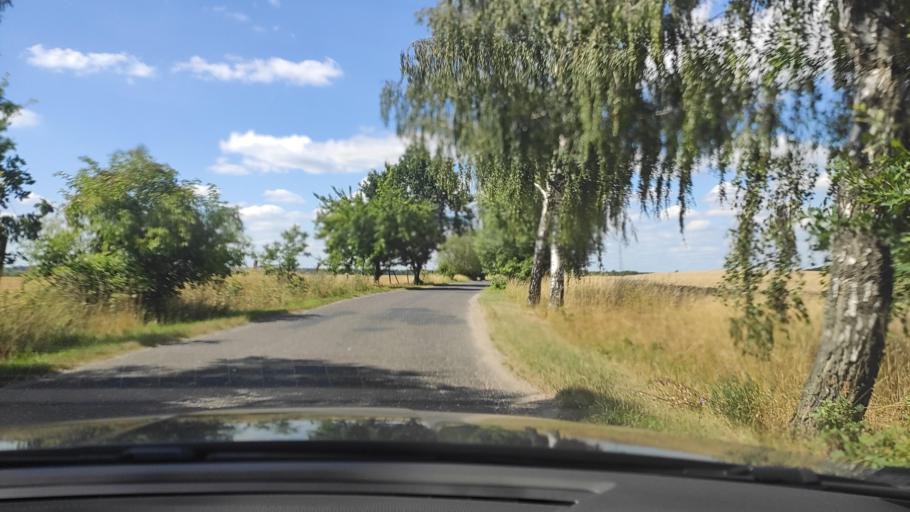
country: PL
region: Greater Poland Voivodeship
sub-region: Powiat poznanski
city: Kobylnica
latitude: 52.4859
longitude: 17.1358
